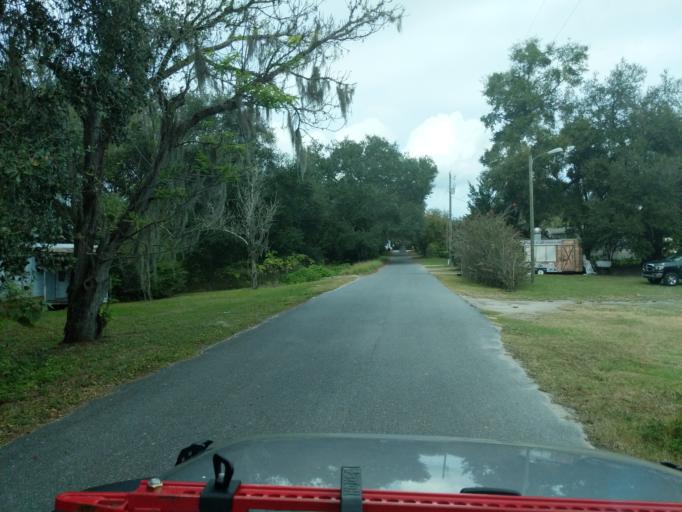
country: US
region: Florida
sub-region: Lake County
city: Mascotte
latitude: 28.5744
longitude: -81.9206
